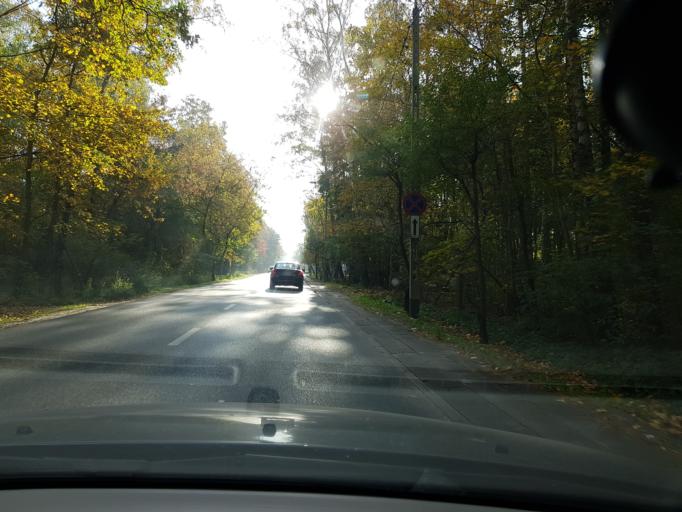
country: PL
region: Masovian Voivodeship
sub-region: Warszawa
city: Bemowo
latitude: 52.2613
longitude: 20.8934
